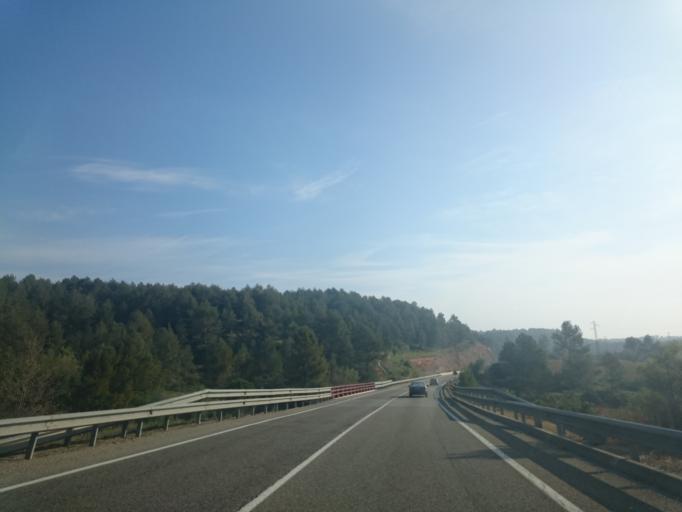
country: ES
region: Catalonia
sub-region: Provincia de Barcelona
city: Sant Salvador de Guardiola
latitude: 41.6862
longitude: 1.7566
